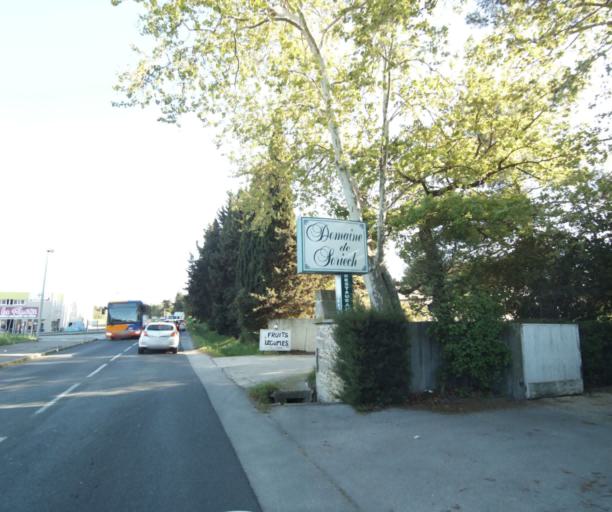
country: FR
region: Languedoc-Roussillon
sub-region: Departement de l'Herault
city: Lattes
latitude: 43.5798
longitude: 3.9218
